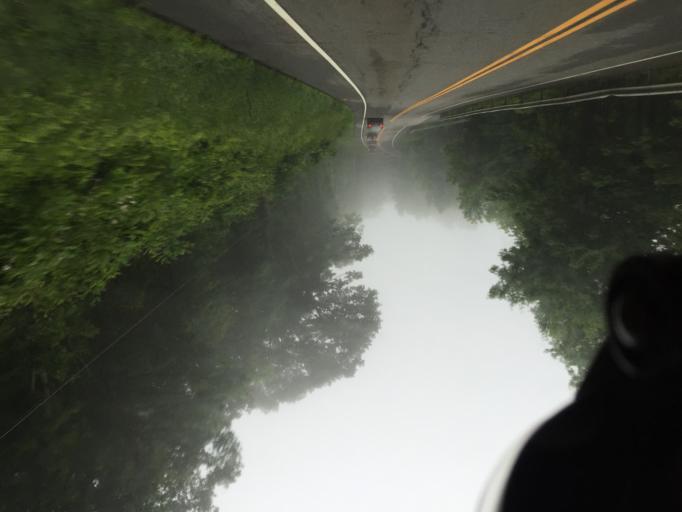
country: US
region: Connecticut
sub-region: Litchfield County
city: Winchester Center
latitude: 41.8823
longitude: -73.2526
